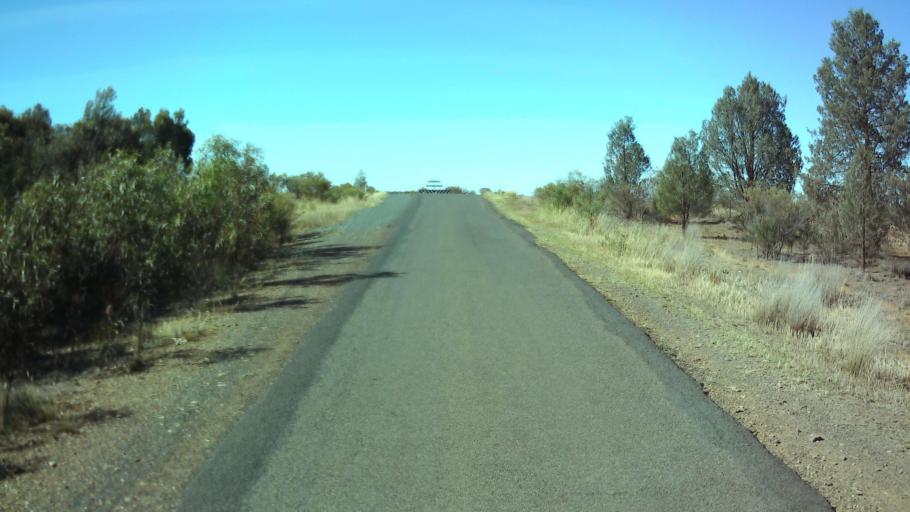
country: AU
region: New South Wales
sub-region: Weddin
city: Grenfell
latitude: -33.7561
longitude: 147.8303
